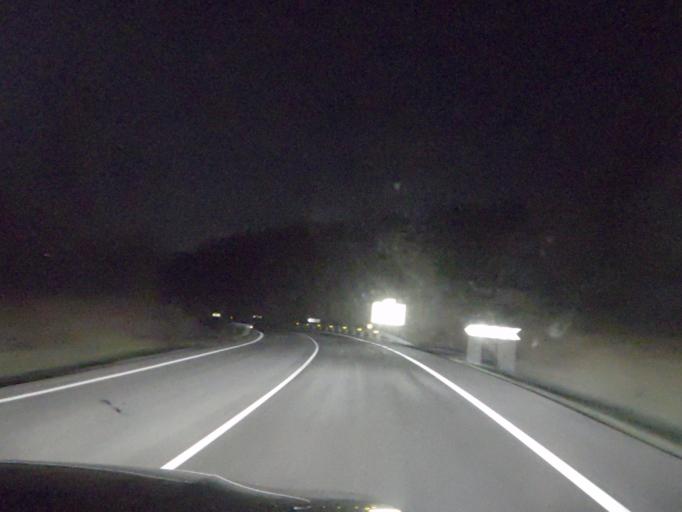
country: ES
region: Galicia
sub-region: Provincia de Ourense
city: Cualedro
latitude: 41.9658
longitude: -7.5172
